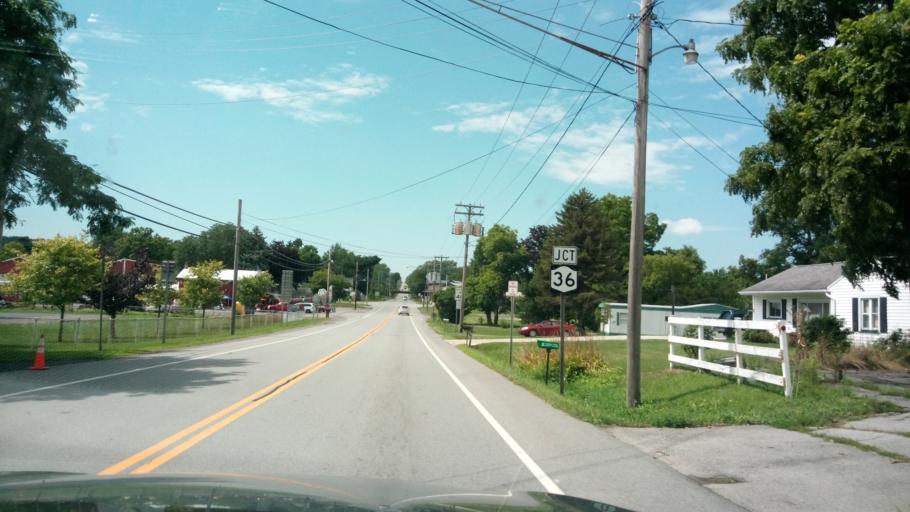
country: US
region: New York
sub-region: Livingston County
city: Geneseo
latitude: 42.8307
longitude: -77.8946
